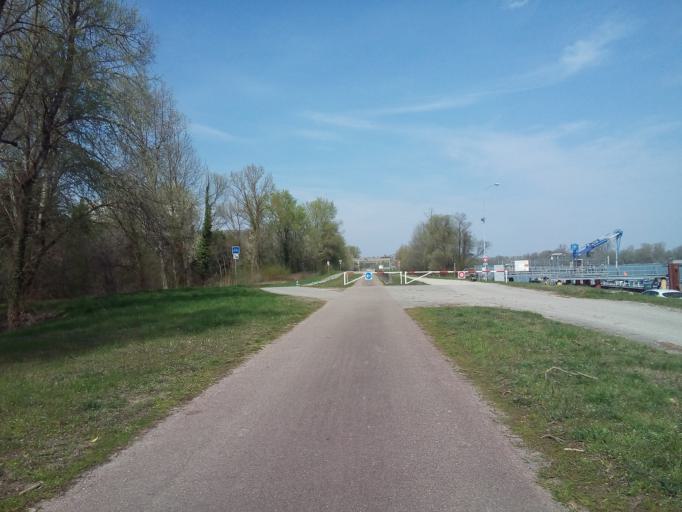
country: FR
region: Alsace
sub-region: Departement du Bas-Rhin
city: Seltz
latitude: 48.8557
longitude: 8.1076
